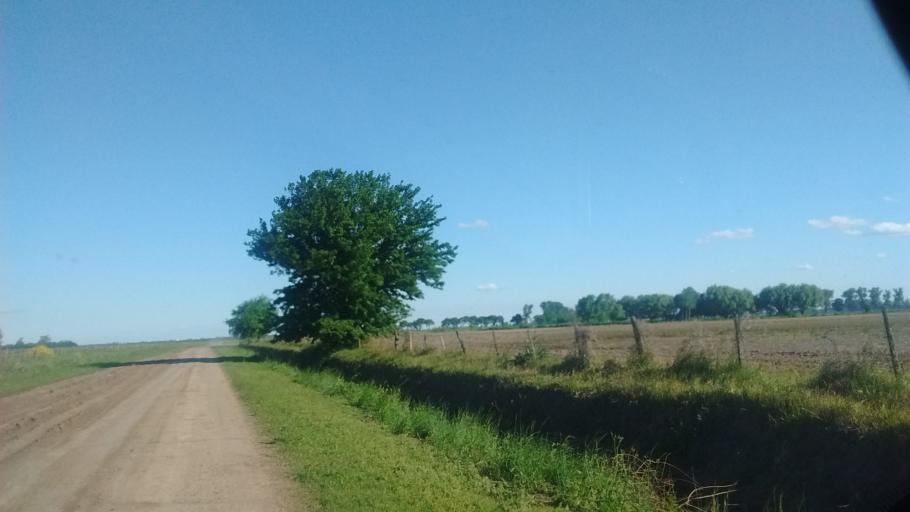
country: AR
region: Santa Fe
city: Funes
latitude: -32.8668
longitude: -60.7997
